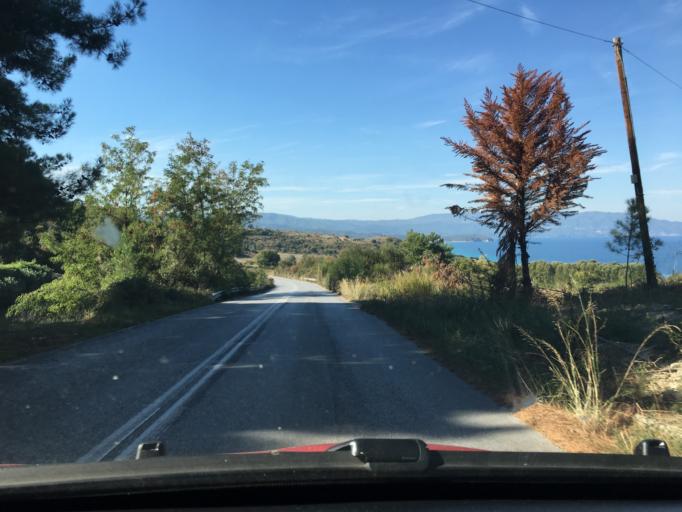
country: GR
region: Central Macedonia
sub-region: Nomos Chalkidikis
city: Ierissos
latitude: 40.3851
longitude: 23.8975
